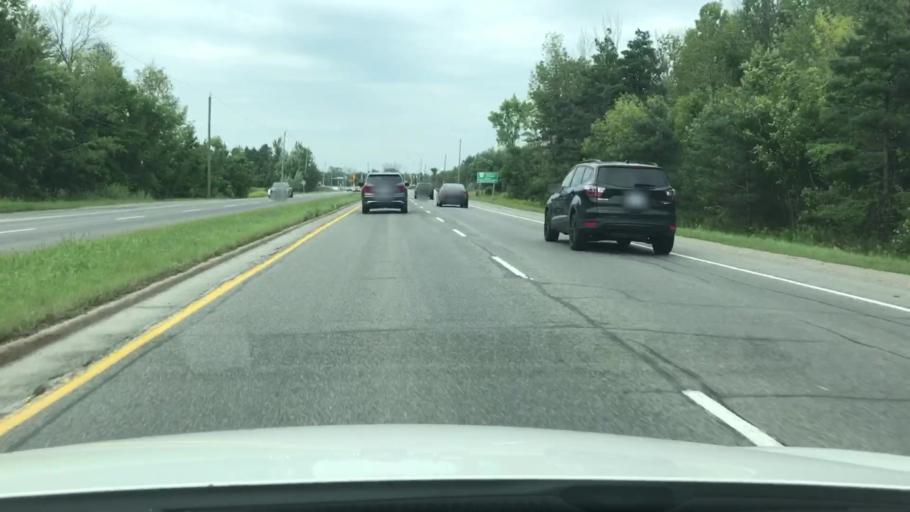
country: CA
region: Ontario
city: Newmarket
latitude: 44.1021
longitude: -79.5161
